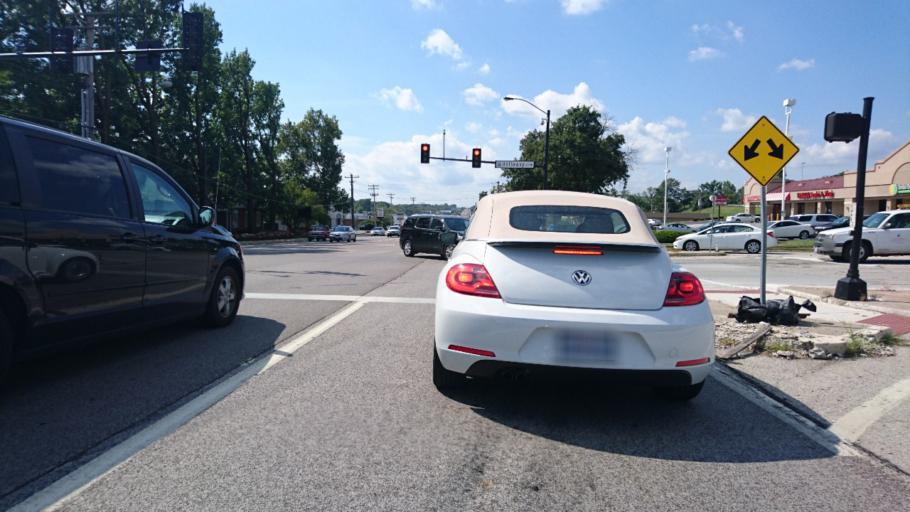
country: US
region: Missouri
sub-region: Saint Louis County
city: Ballwin
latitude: 38.5930
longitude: -90.5460
